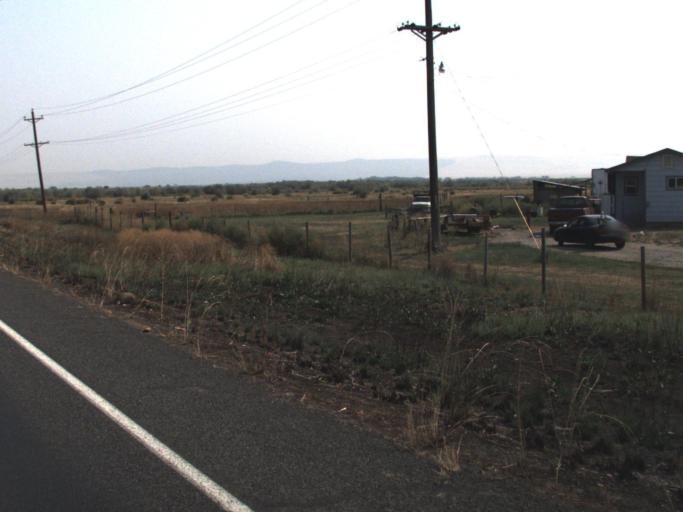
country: US
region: Washington
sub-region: Yakima County
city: Granger
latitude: 46.2680
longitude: -120.1466
